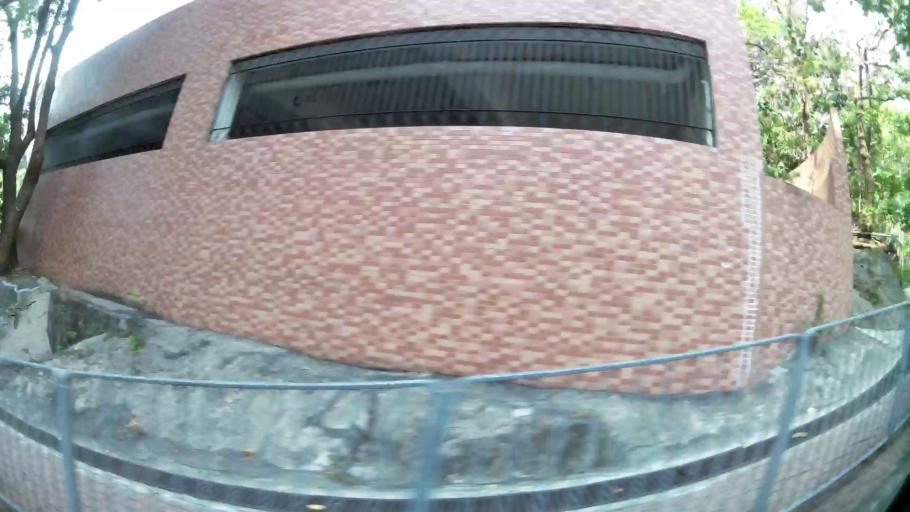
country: HK
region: Wanchai
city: Wan Chai
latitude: 22.2737
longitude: 114.1850
